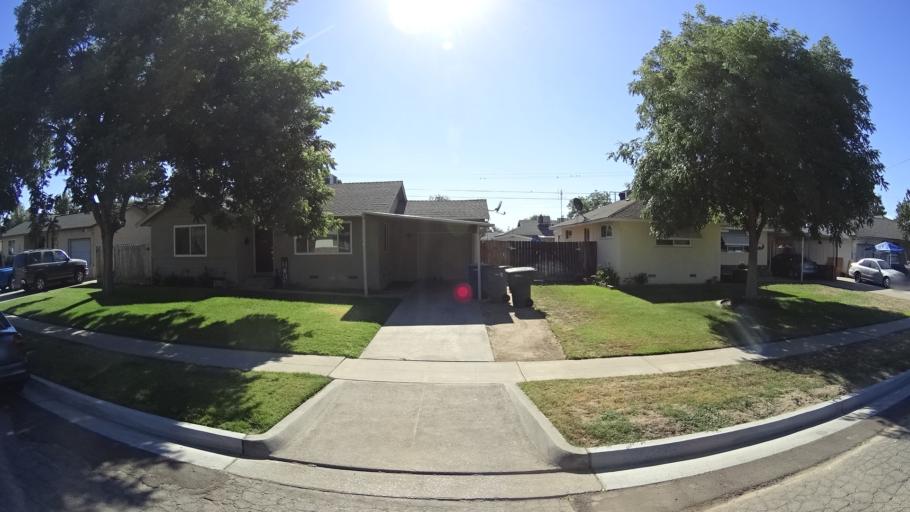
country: US
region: California
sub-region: Fresno County
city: Fresno
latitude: 36.7913
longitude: -119.8304
